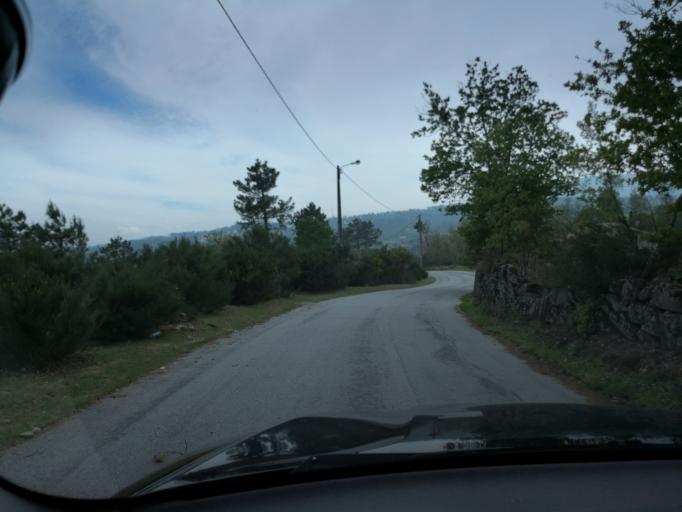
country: PT
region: Vila Real
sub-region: Vila Real
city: Vila Real
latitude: 41.2885
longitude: -7.8063
